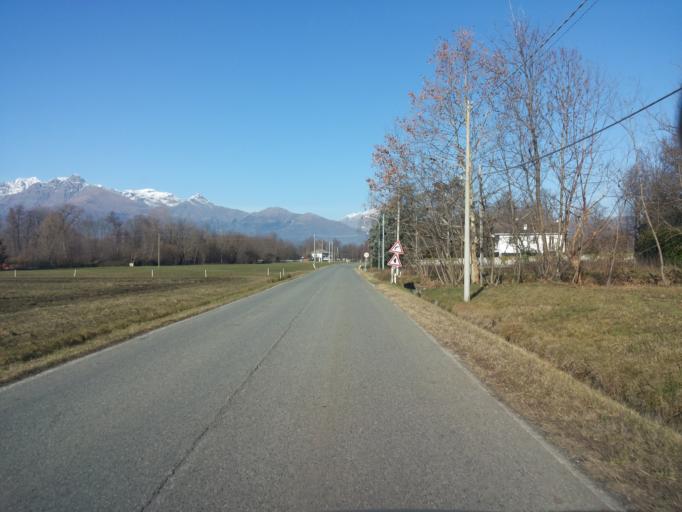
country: IT
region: Piedmont
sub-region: Provincia di Biella
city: Ponderano
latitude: 45.5239
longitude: 8.0524
